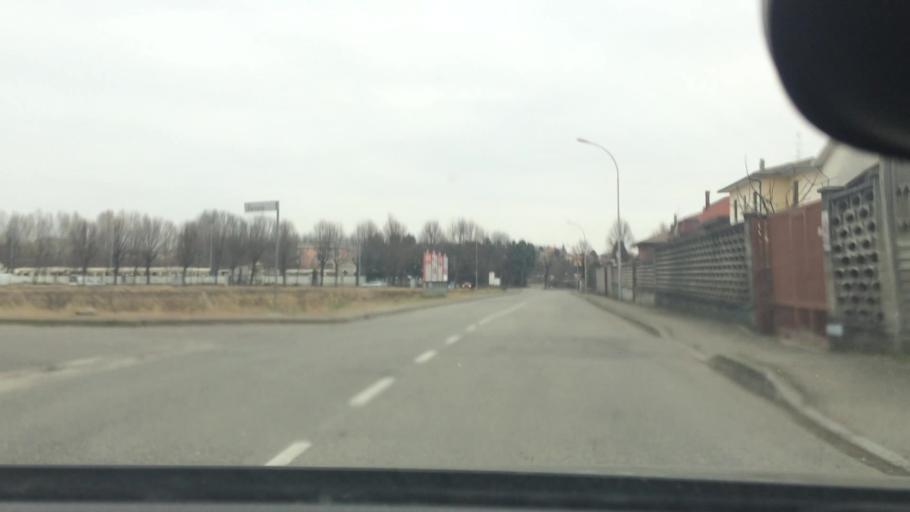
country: IT
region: Lombardy
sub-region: Citta metropolitana di Milano
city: Solaro
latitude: 45.6198
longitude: 9.0786
